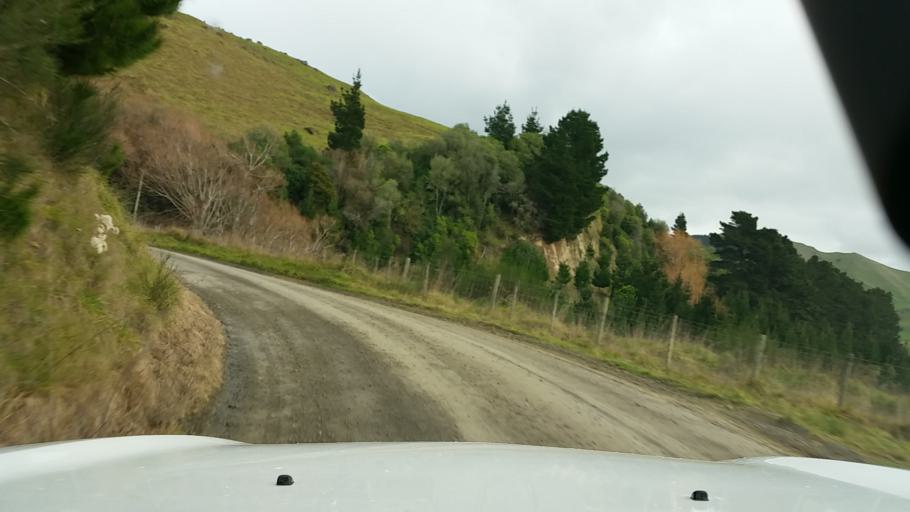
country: NZ
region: Wellington
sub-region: South Wairarapa District
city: Waipawa
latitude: -41.2163
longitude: 175.5811
